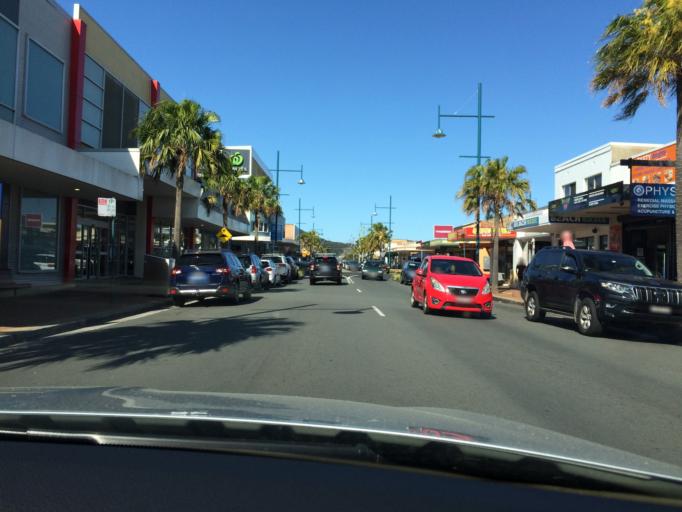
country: AU
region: New South Wales
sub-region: Gosford Shire
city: Umina
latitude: -33.5216
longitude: 151.3202
